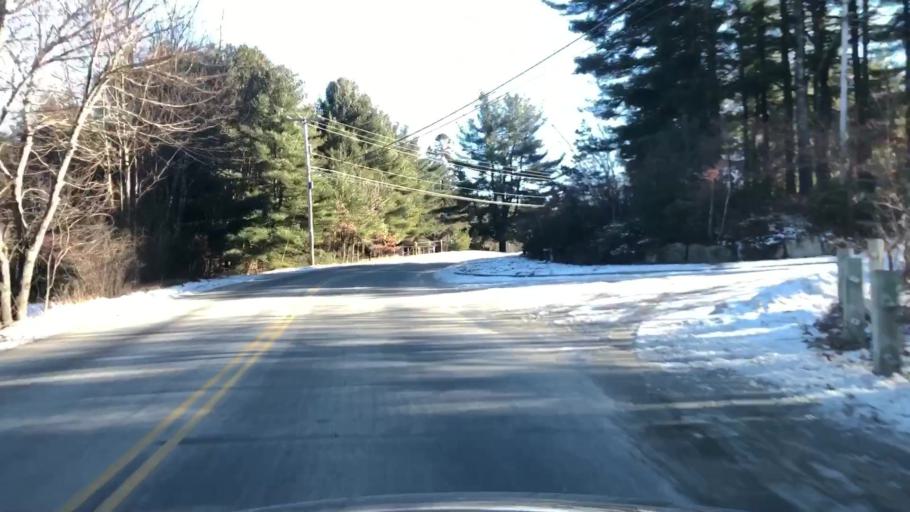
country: US
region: New Hampshire
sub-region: Hillsborough County
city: Milford
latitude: 42.8169
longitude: -71.6575
